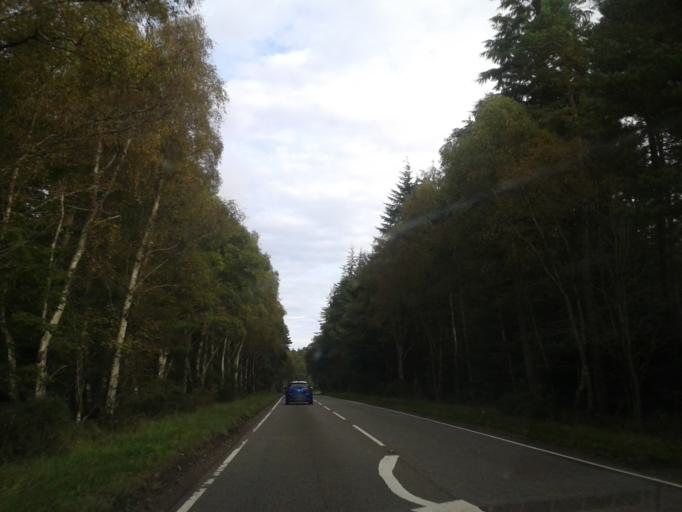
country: GB
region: Scotland
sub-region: Moray
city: Fochabers
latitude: 57.6229
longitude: -3.0542
